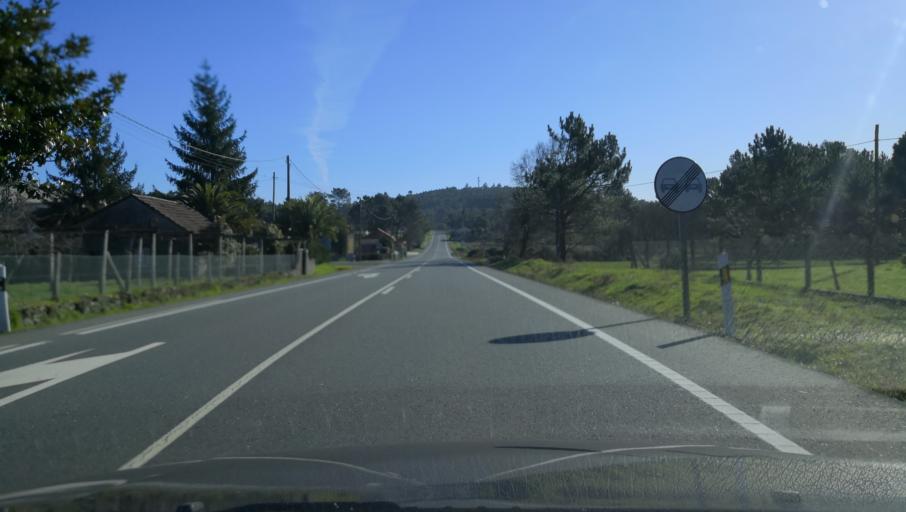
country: ES
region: Galicia
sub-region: Provincia da Coruna
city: Ribeira
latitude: 42.7564
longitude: -8.3625
